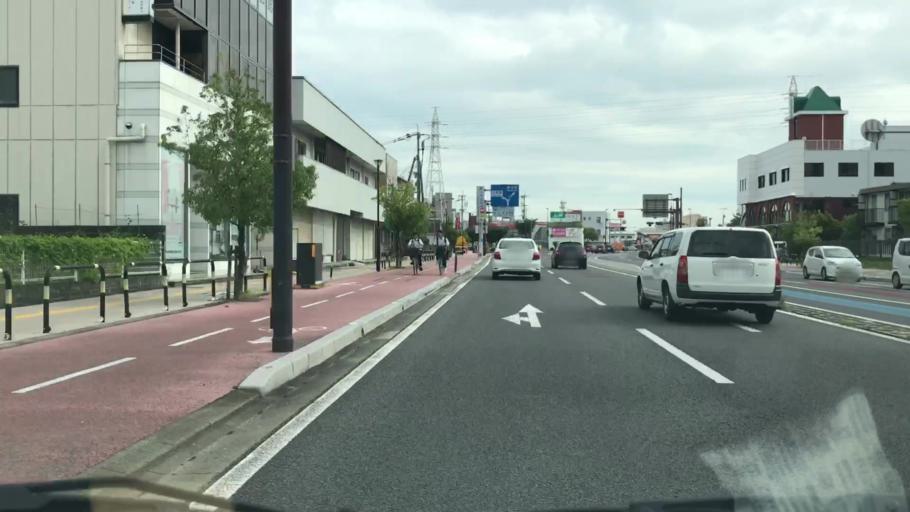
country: JP
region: Saga Prefecture
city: Saga-shi
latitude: 33.2740
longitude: 130.2939
